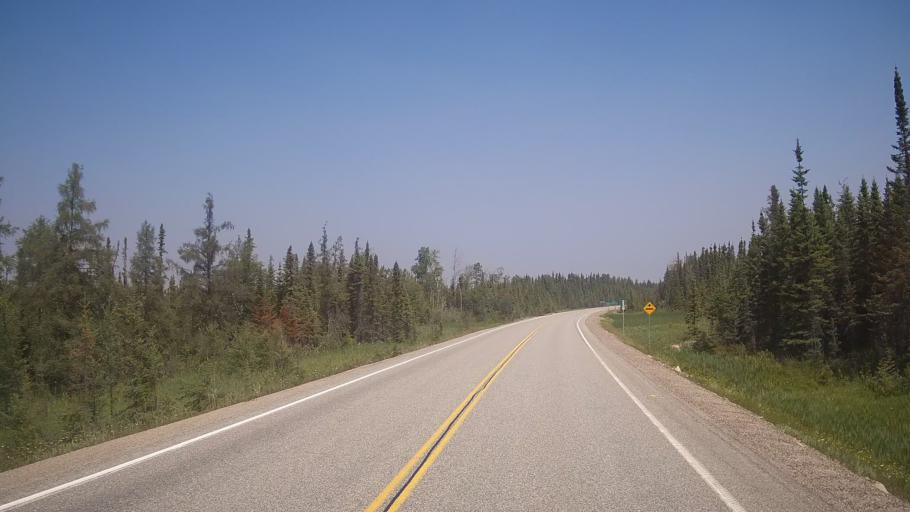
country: CA
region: Ontario
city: Timmins
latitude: 48.1899
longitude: -81.5835
